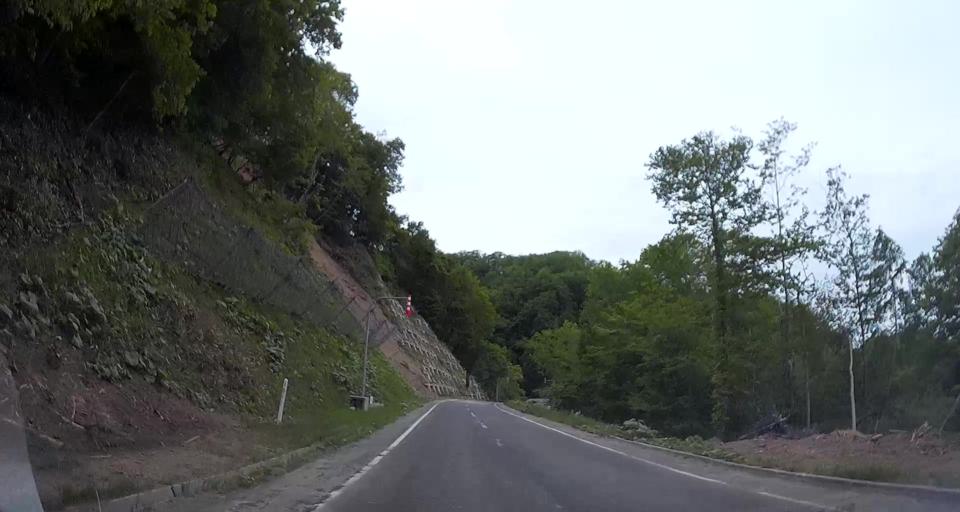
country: JP
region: Hokkaido
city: Chitose
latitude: 42.7883
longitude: 142.0487
